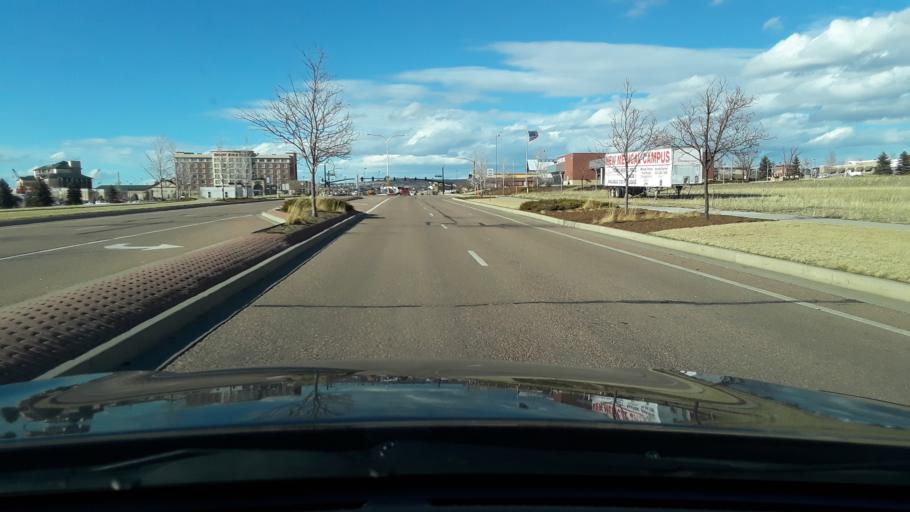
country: US
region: Colorado
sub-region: El Paso County
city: Air Force Academy
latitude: 38.9888
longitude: -104.8077
